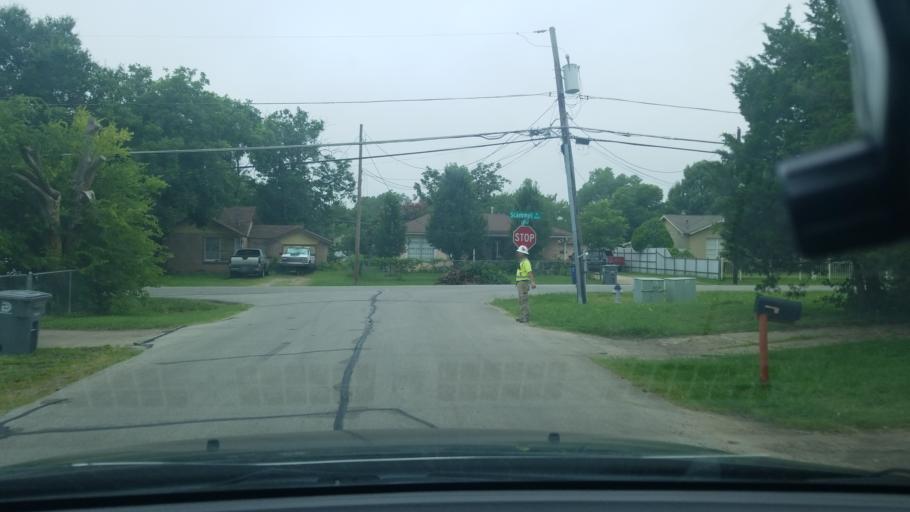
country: US
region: Texas
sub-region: Dallas County
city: Balch Springs
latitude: 32.7568
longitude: -96.6769
